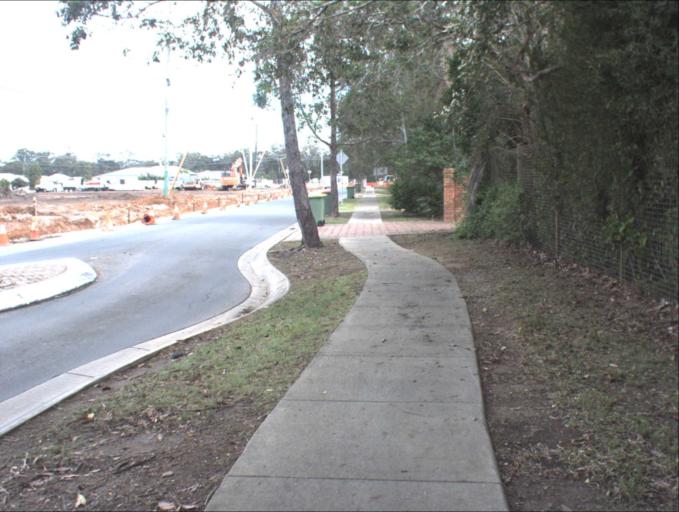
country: AU
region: Queensland
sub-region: Logan
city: Park Ridge South
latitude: -27.6705
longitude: 153.0245
